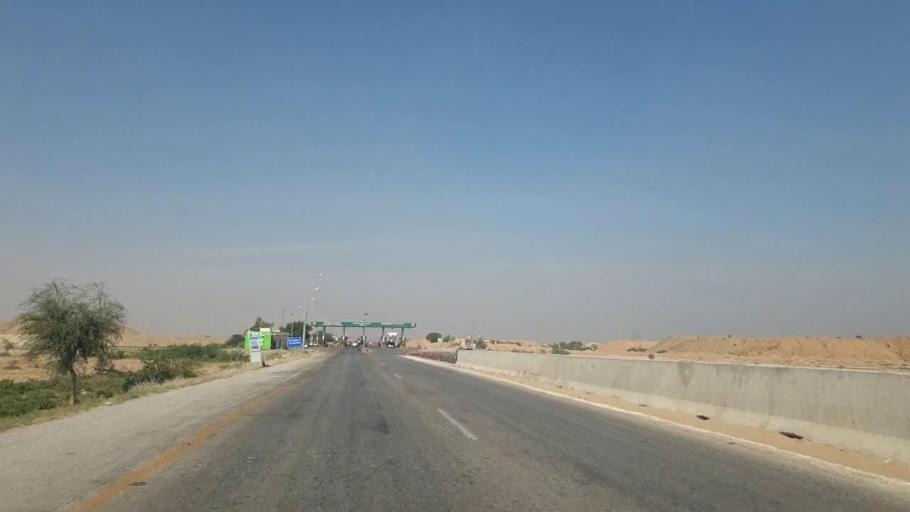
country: PK
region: Sindh
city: Matiari
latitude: 25.5771
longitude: 68.3136
